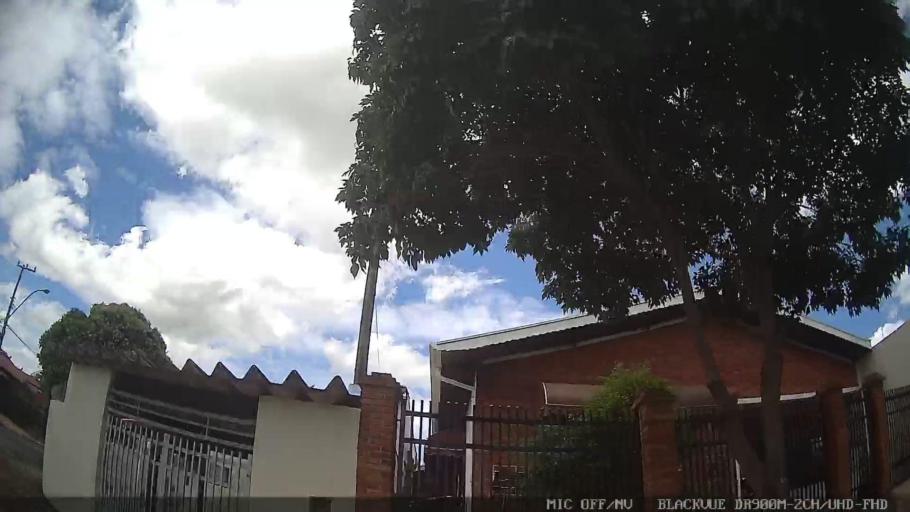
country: BR
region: Sao Paulo
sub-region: Jaguariuna
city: Jaguariuna
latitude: -22.7141
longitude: -46.9806
